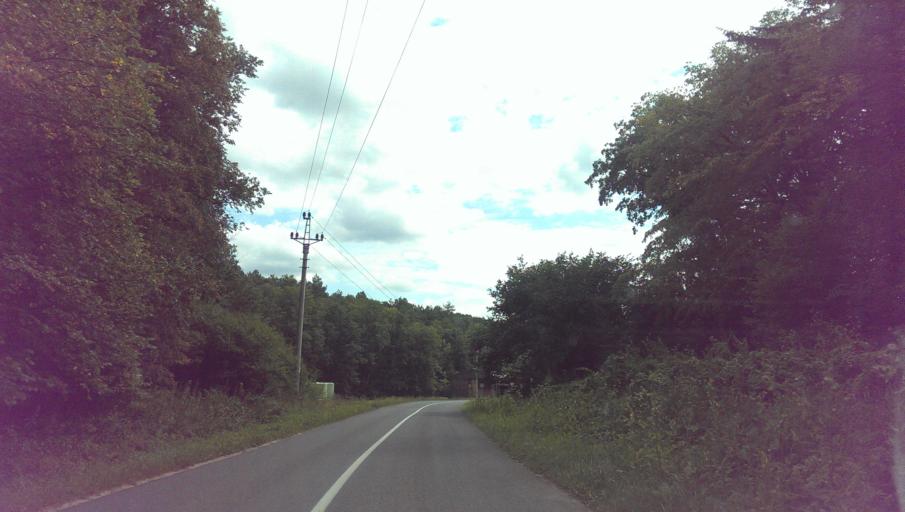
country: CZ
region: South Moravian
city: Velka nad Velickou
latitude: 48.8965
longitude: 17.5740
